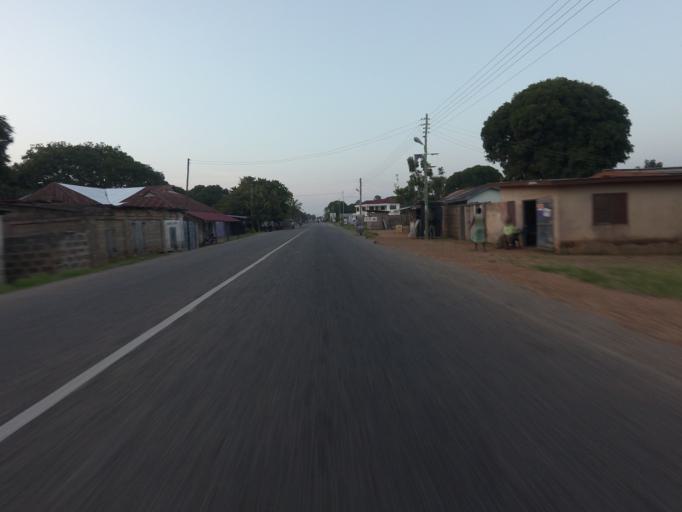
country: GH
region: Volta
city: Keta
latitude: 5.8699
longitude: 0.9793
